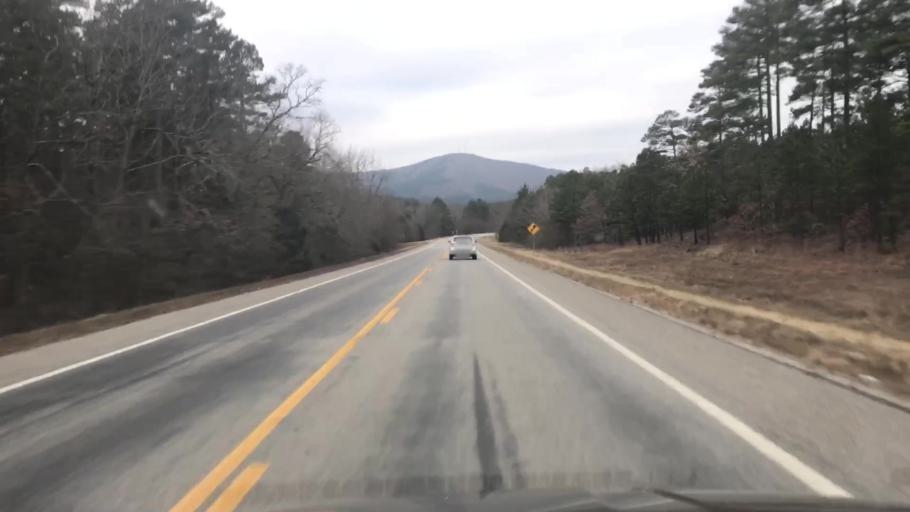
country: US
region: Arkansas
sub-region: Montgomery County
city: Mount Ida
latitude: 34.6877
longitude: -93.8872
